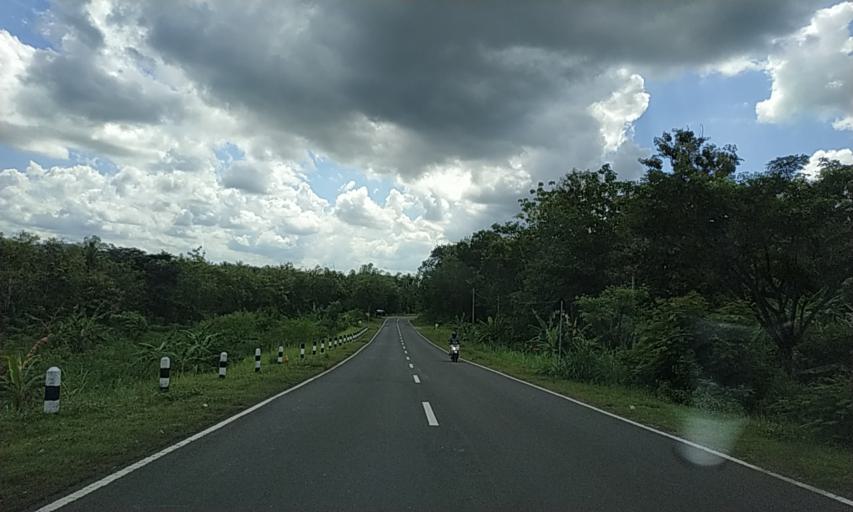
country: ID
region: East Java
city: Krajan
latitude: -8.0408
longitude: 110.9454
